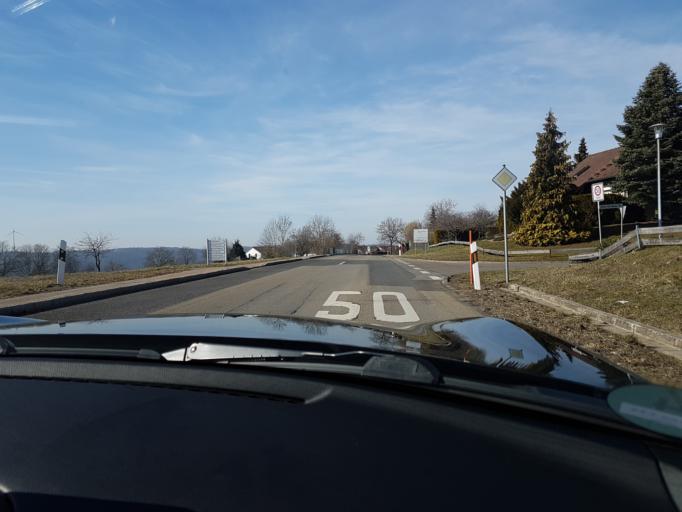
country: DE
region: Baden-Wuerttemberg
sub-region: Regierungsbezirk Stuttgart
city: Langenburg
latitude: 49.2499
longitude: 9.8608
